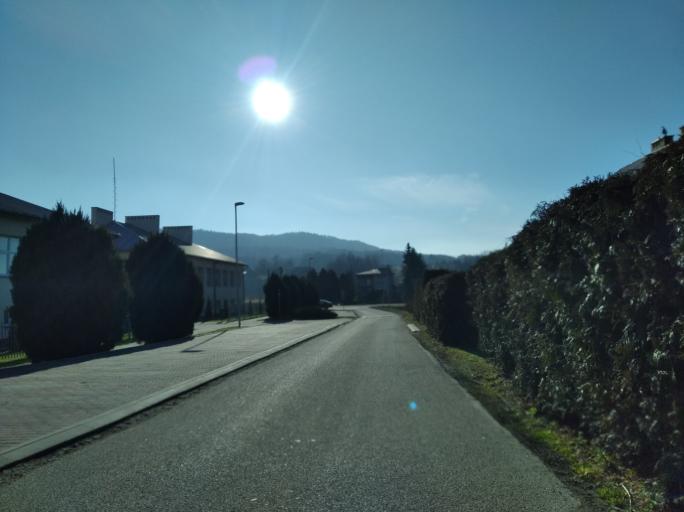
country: PL
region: Subcarpathian Voivodeship
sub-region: Powiat strzyzowski
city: Jawornik
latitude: 49.8059
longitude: 21.8898
